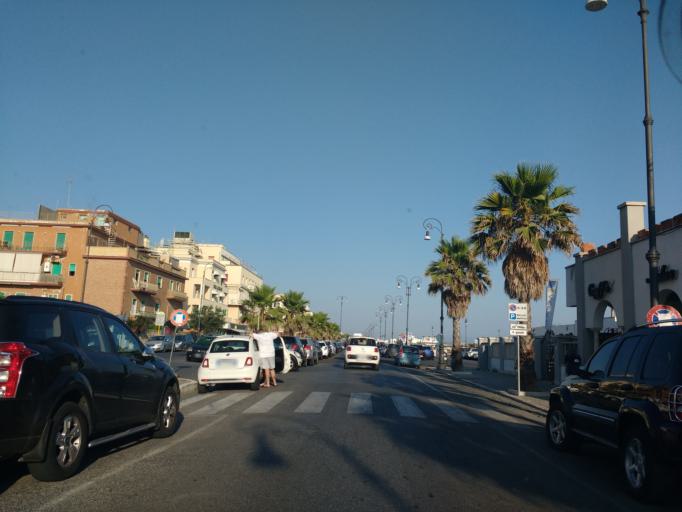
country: IT
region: Latium
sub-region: Citta metropolitana di Roma Capitale
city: Lido di Ostia
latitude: 41.7303
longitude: 12.2745
